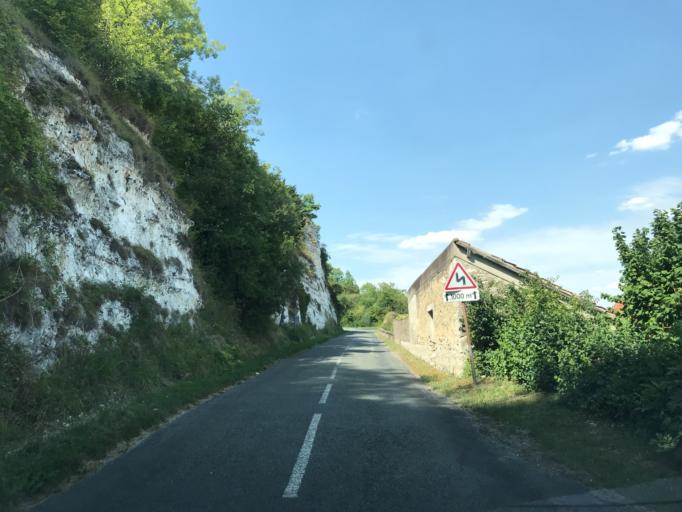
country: FR
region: Ile-de-France
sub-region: Departement des Yvelines
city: Freneuse
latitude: 49.0604
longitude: 1.5995
